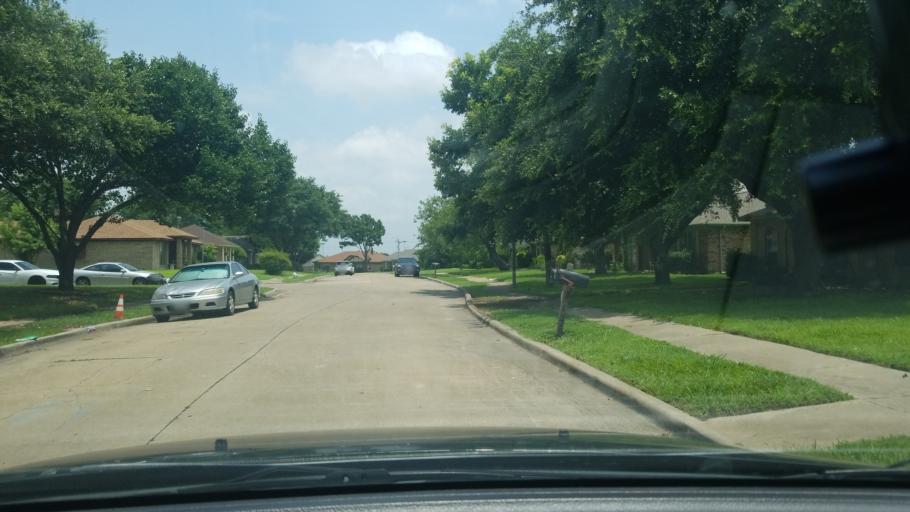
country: US
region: Texas
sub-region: Dallas County
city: Mesquite
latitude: 32.7979
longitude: -96.6137
